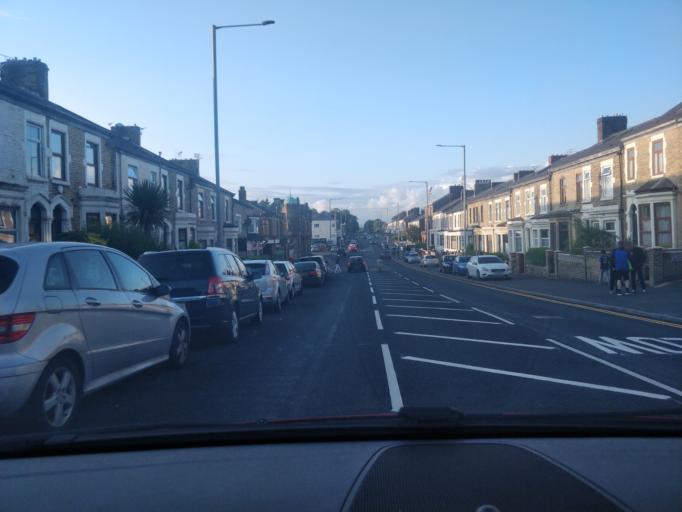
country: GB
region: England
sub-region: Lancashire
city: Preston
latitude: 53.7673
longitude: -2.6917
